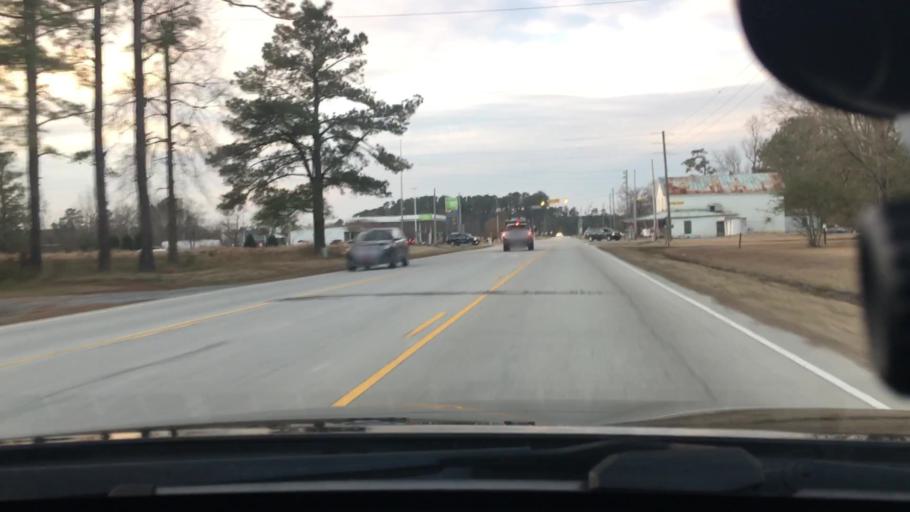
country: US
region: North Carolina
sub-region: Pitt County
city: Windsor
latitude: 35.4636
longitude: -77.2738
